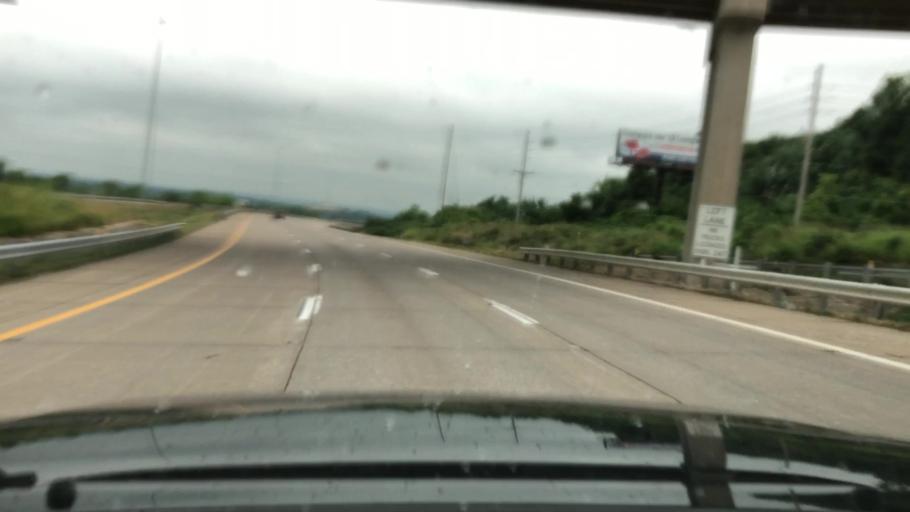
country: US
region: Missouri
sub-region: Saint Charles County
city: Saint Peters
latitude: 38.8009
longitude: -90.5898
